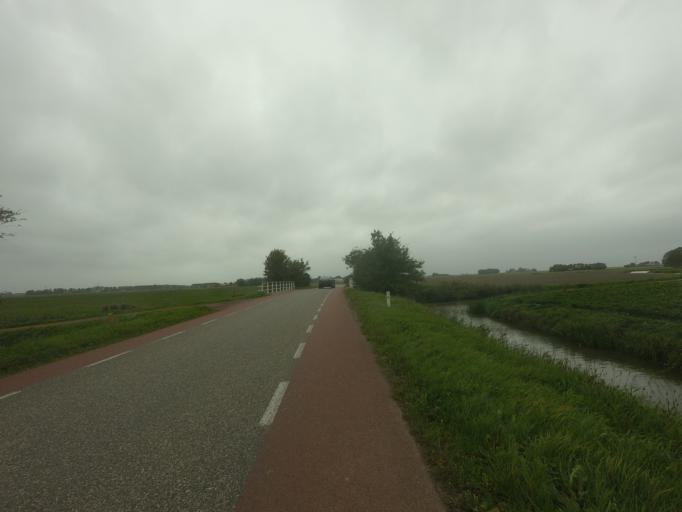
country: NL
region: Friesland
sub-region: Gemeente Ferwerderadiel
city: Ferwert
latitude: 53.3346
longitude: 5.8473
